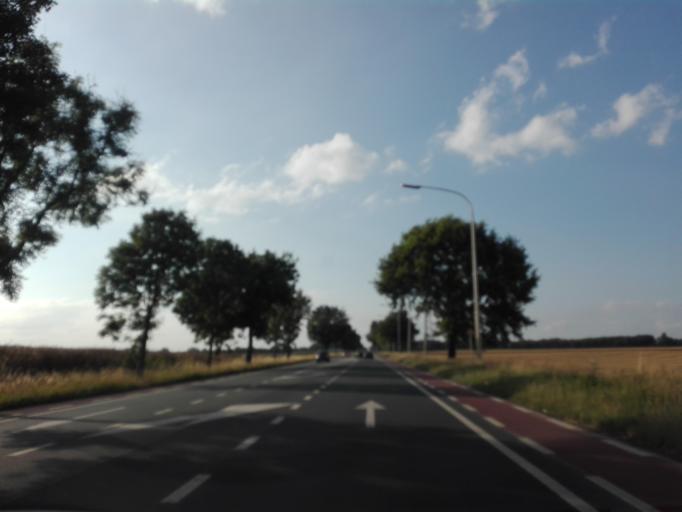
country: BE
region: Wallonia
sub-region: Province du Brabant Wallon
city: Louvain-la-Neuve
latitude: 50.6505
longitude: 4.6412
